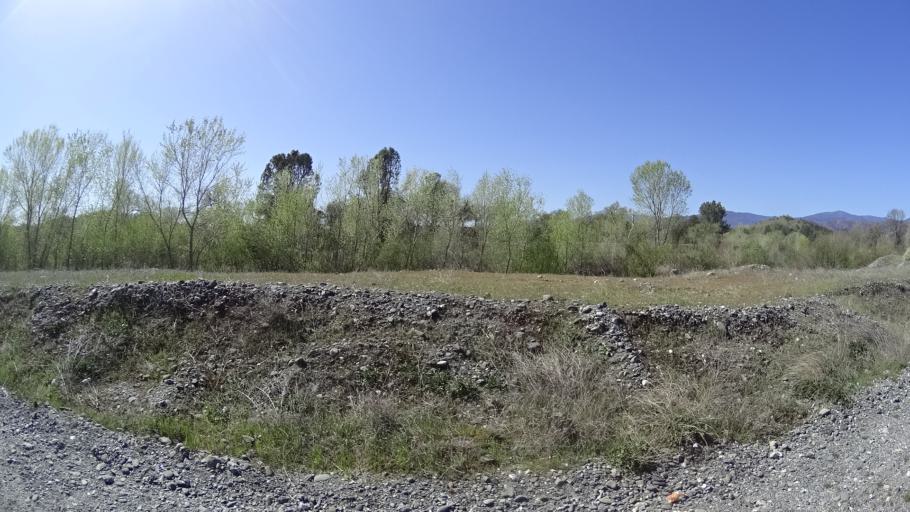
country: US
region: California
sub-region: Glenn County
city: Orland
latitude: 39.6799
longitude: -122.5284
